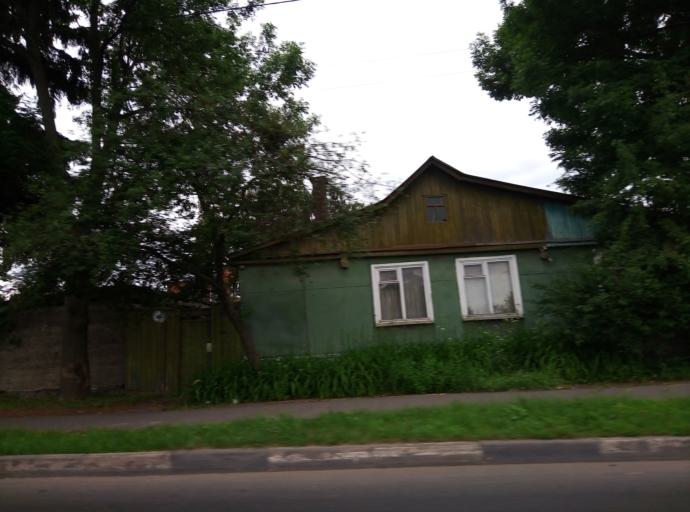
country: RU
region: Kursk
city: Kursk
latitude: 51.7333
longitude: 36.1548
